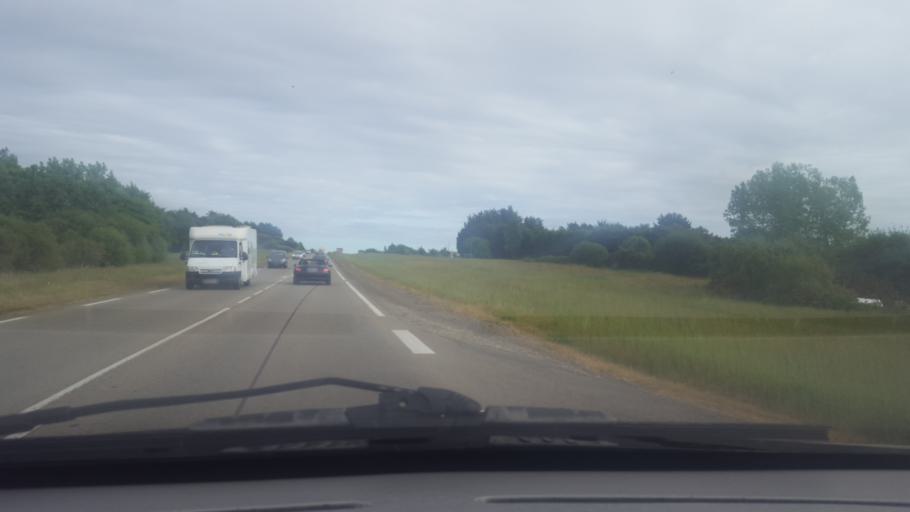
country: FR
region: Pays de la Loire
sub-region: Departement de la Loire-Atlantique
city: Les Moutiers-en-Retz
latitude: 47.0585
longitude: -1.9759
